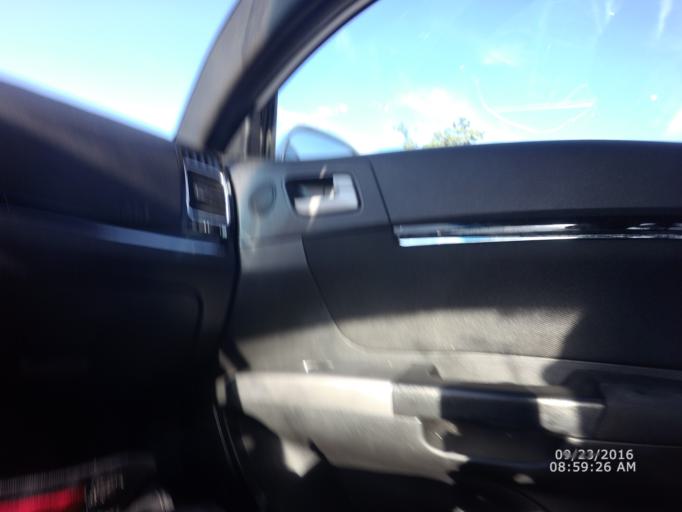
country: CU
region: La Habana
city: Diez de Octubre
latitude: 23.0705
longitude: -82.3988
